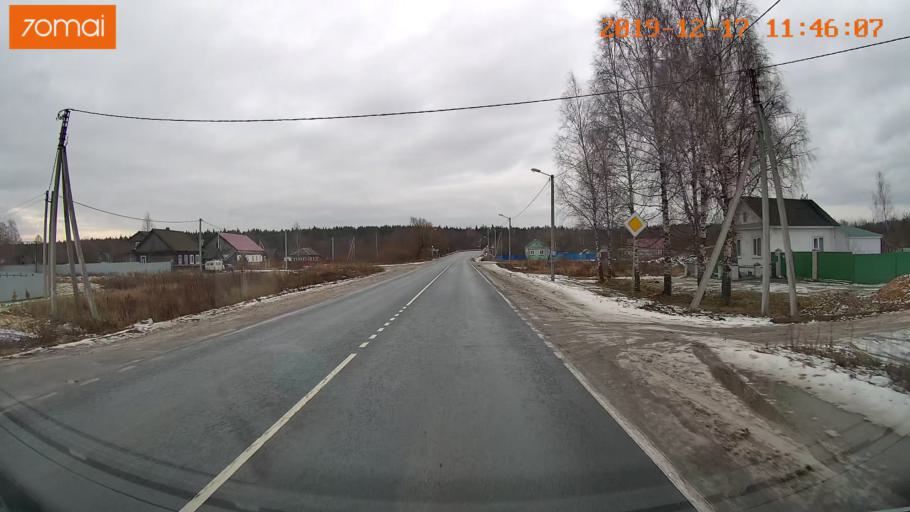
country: RU
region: Vladimir
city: Velikodvorskiy
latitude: 55.2450
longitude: 40.6753
